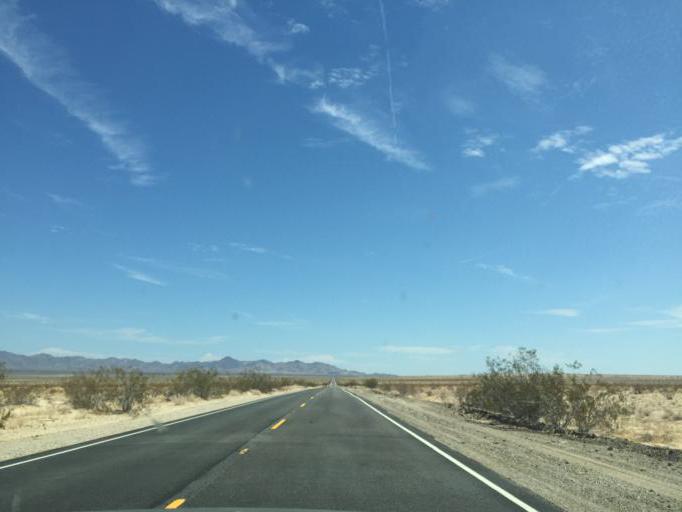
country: US
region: California
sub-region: Riverside County
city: Mesa Verde
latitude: 34.0997
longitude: -115.0042
